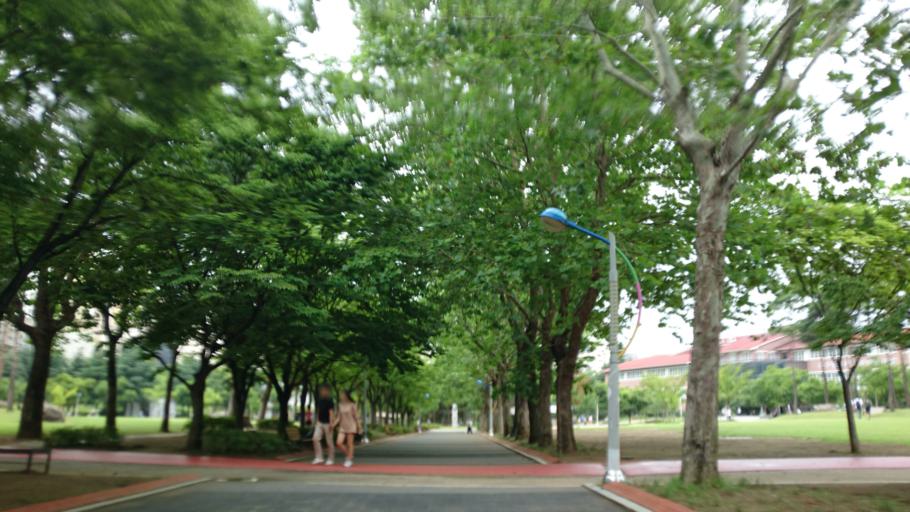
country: KR
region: Daegu
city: Daegu
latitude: 35.8711
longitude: 128.6406
